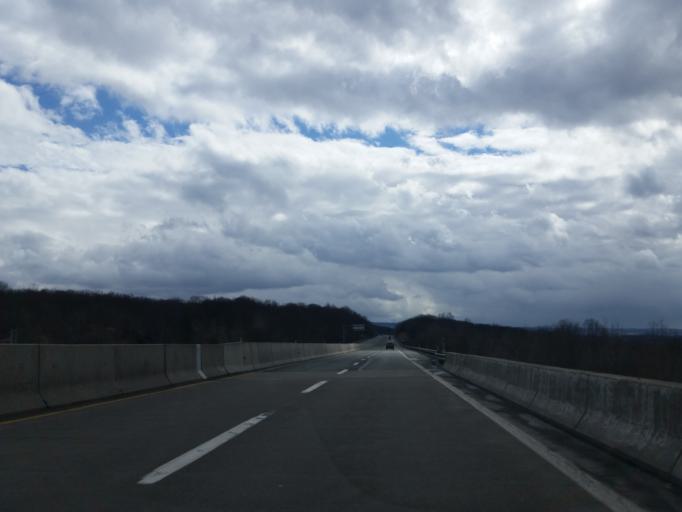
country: US
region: Pennsylvania
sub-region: Lackawanna County
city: Old Forge
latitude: 41.3744
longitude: -75.7204
